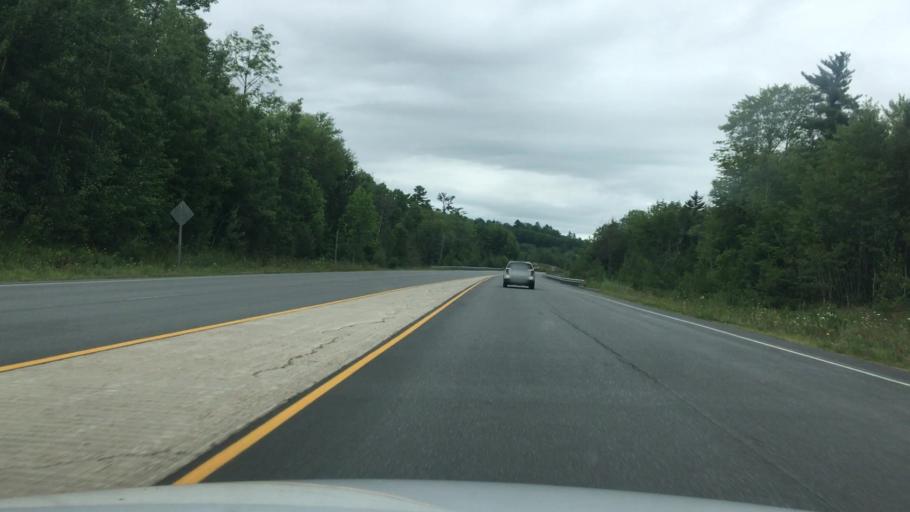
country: US
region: Maine
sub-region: Hancock County
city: Franklin
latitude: 44.8522
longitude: -68.3283
